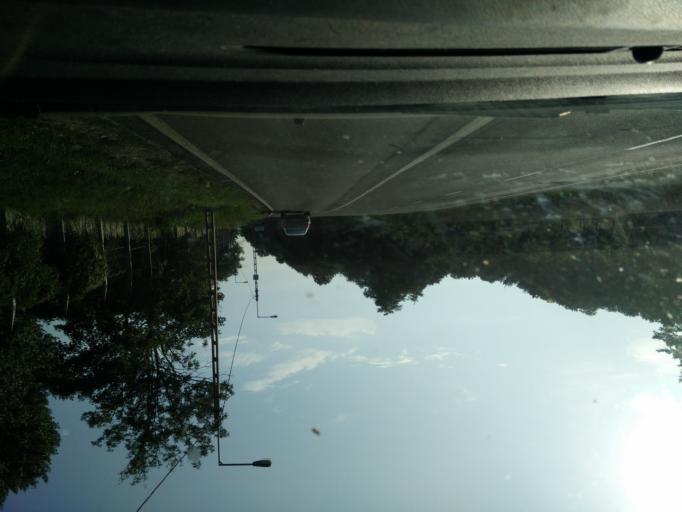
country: HU
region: Pest
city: Piliscsaba
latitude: 47.6291
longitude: 18.8494
